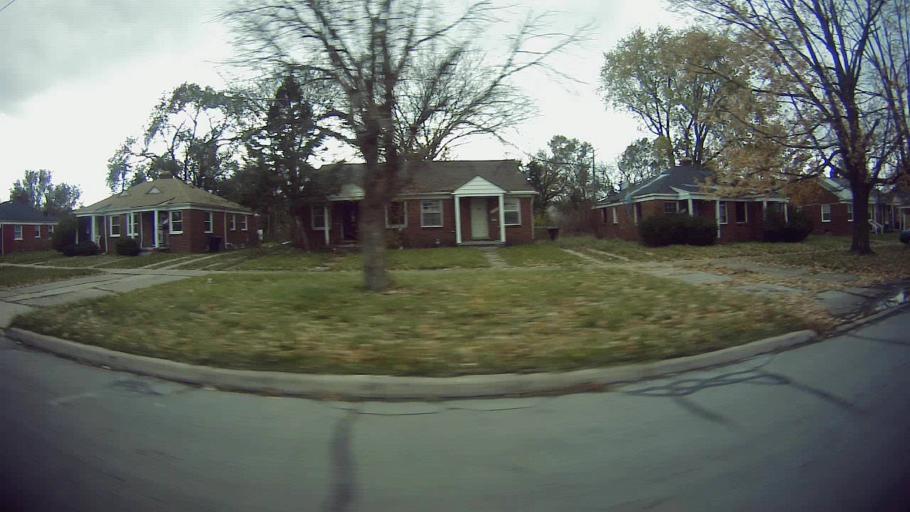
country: US
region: Michigan
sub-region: Wayne County
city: Hamtramck
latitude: 42.4230
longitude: -83.0042
